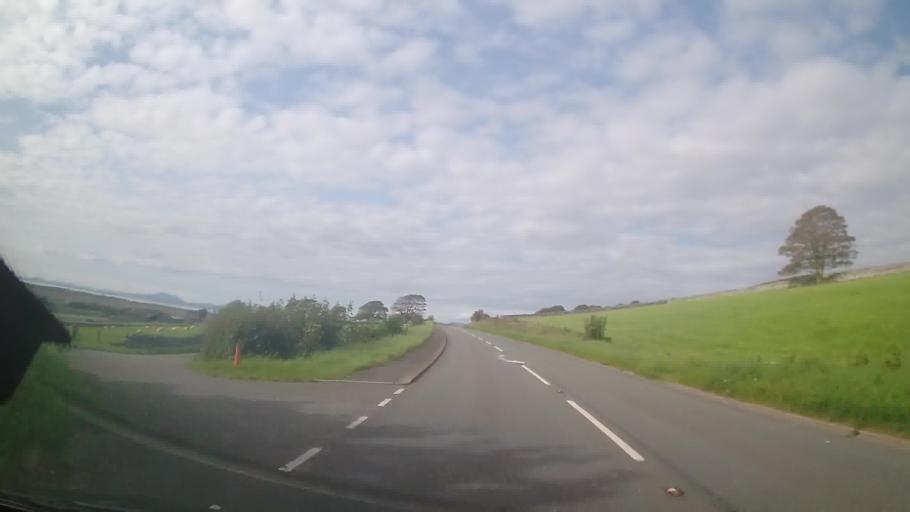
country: GB
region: Wales
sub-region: Gwynedd
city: Llanbedr
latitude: 52.8019
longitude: -4.1016
